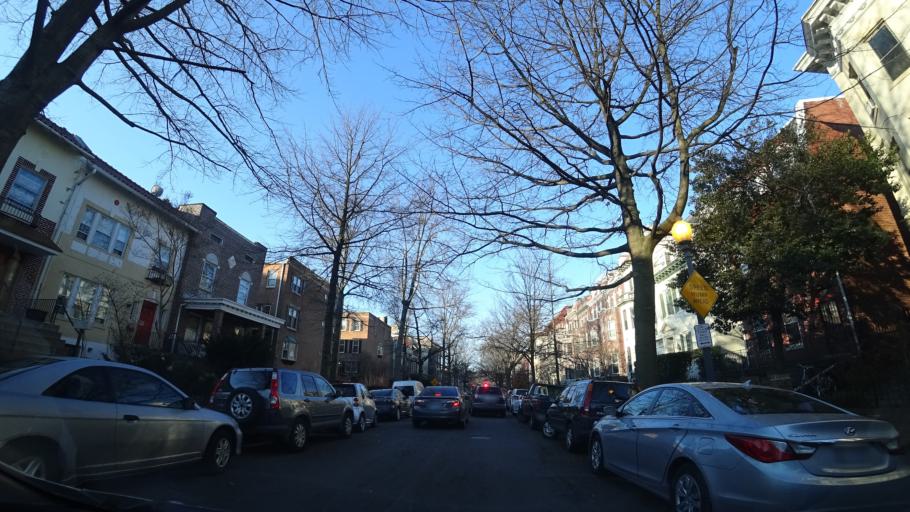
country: US
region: Washington, D.C.
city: Washington, D.C.
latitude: 38.9245
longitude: -77.0424
